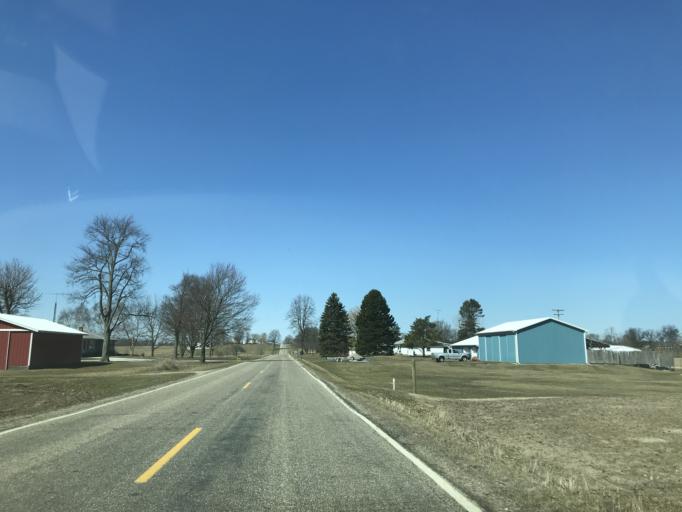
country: US
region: Michigan
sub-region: Hillsdale County
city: Jonesville
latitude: 41.9855
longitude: -84.7042
